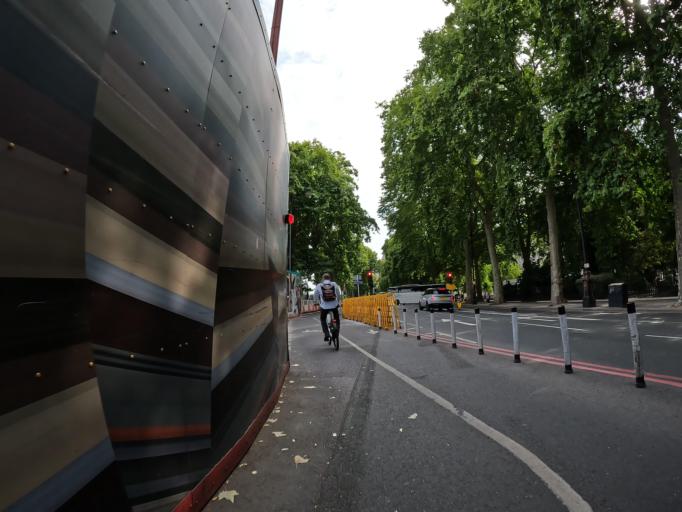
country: GB
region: England
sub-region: Greater London
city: Blackheath
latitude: 51.4448
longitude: 0.0018
